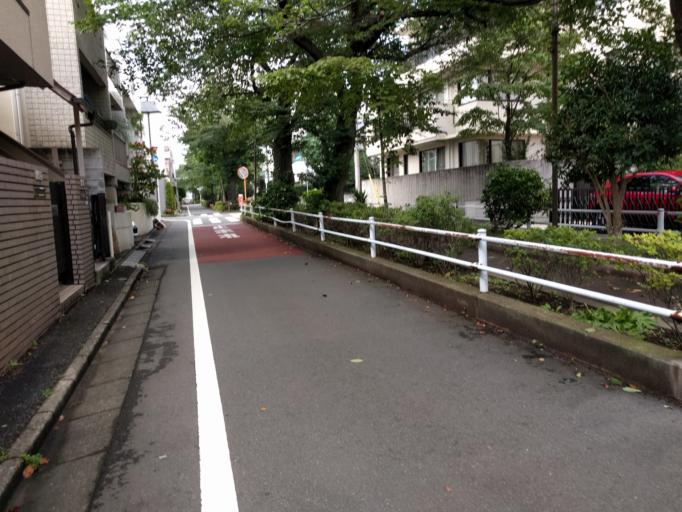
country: JP
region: Tokyo
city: Tokyo
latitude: 35.6223
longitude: 139.6769
